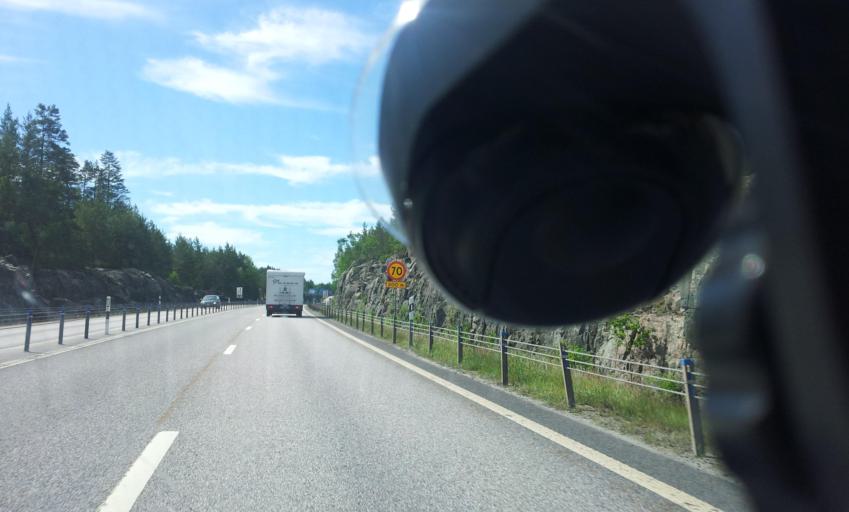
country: SE
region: OEstergoetland
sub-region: Valdemarsviks Kommun
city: Valdemarsvik
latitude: 58.1638
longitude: 16.5417
